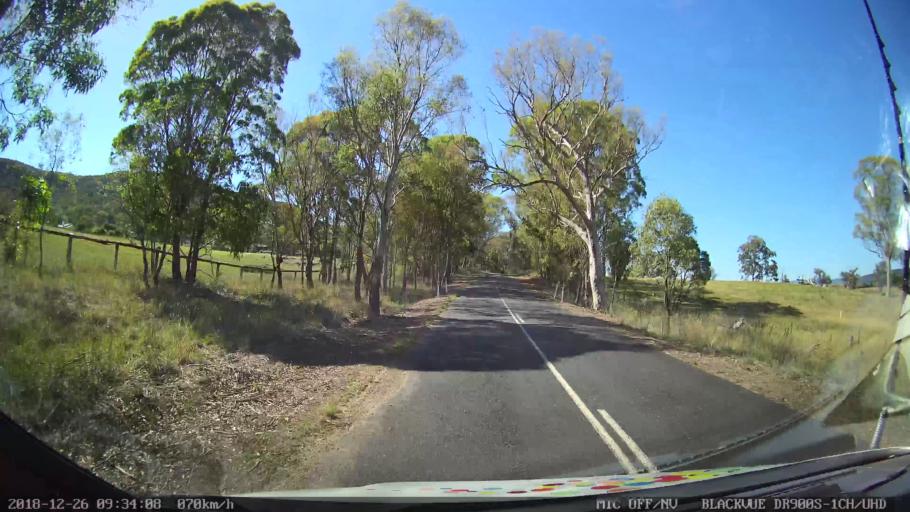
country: AU
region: New South Wales
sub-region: Mid-Western Regional
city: Kandos
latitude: -32.9021
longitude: 150.0373
